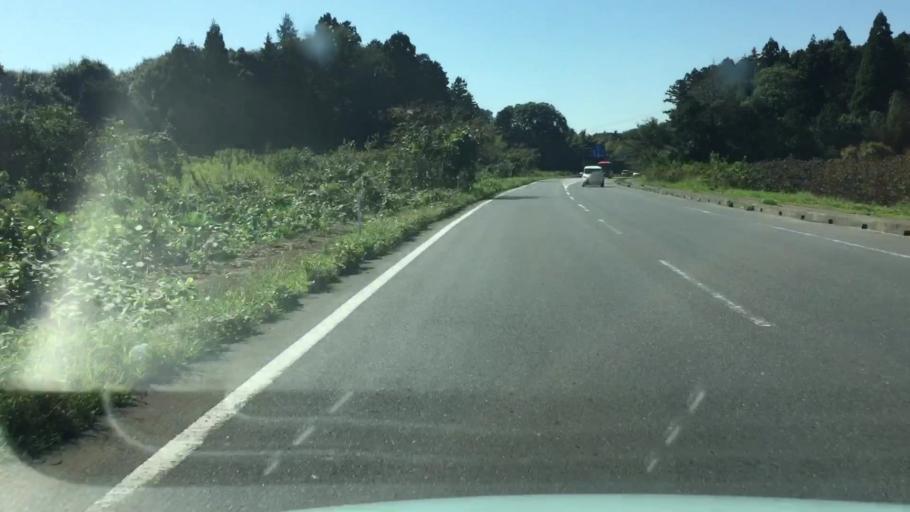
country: JP
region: Ibaraki
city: Ushiku
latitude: 35.9775
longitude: 140.1847
